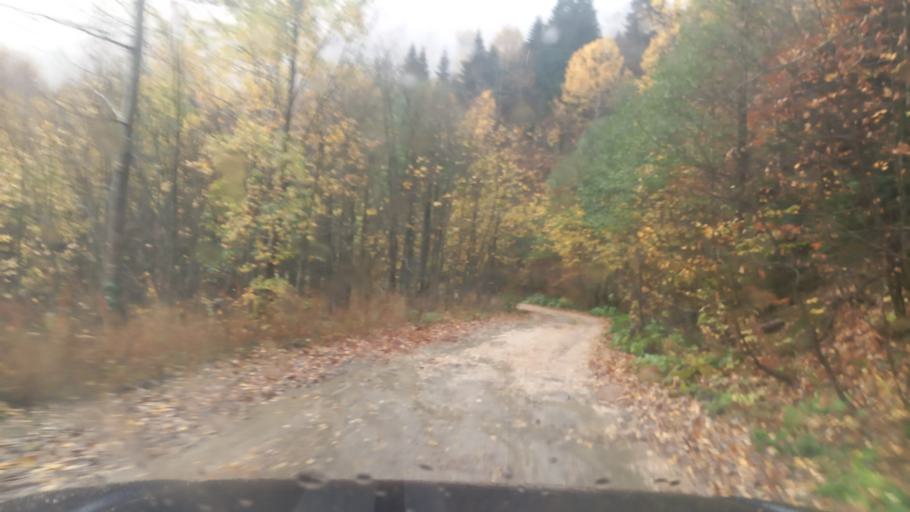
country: RU
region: Krasnodarskiy
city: Neftegorsk
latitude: 44.0144
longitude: 39.8427
